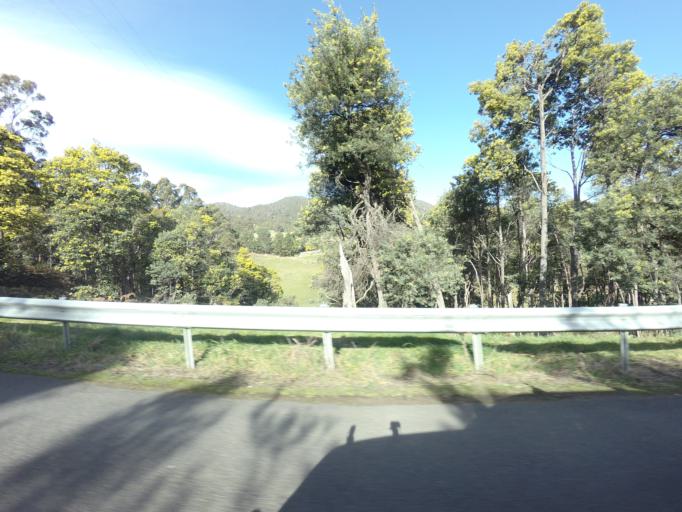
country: AU
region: Tasmania
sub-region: Huon Valley
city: Cygnet
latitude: -43.1738
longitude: 147.1631
